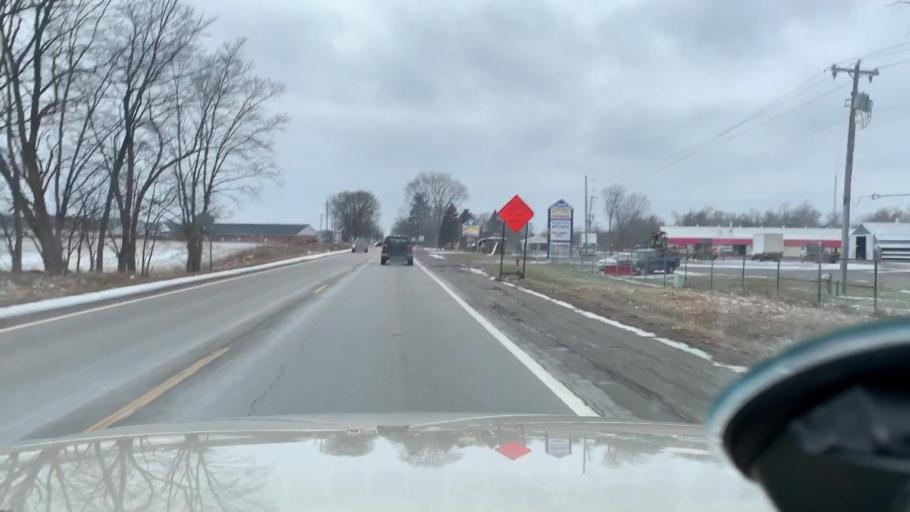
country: US
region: Michigan
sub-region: Jackson County
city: Spring Arbor
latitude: 42.2100
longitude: -84.5330
